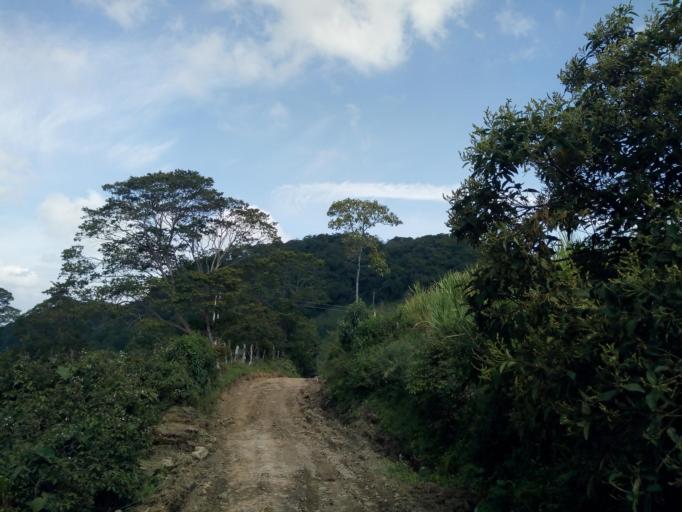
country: CO
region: Boyaca
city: Moniquira
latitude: 5.8695
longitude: -73.5049
